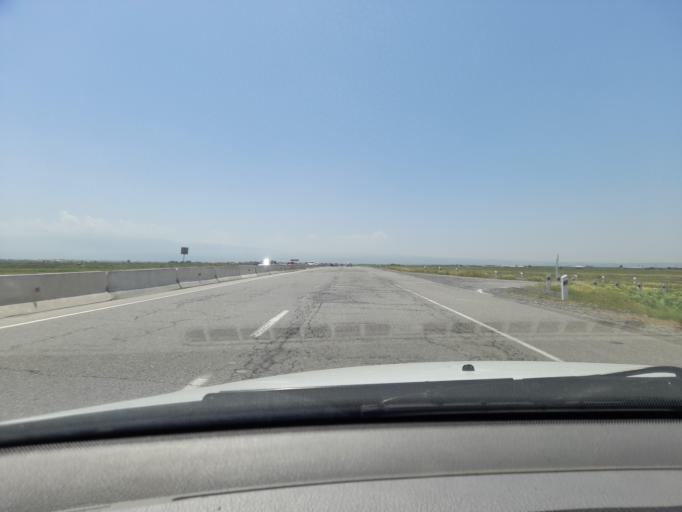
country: UZ
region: Jizzax
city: Paxtakor
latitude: 40.2017
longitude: 67.9777
